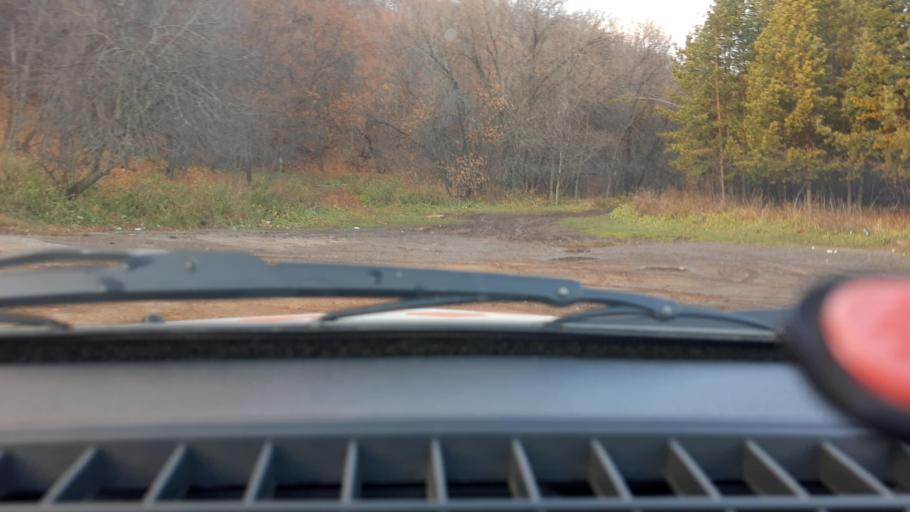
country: RU
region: Bashkortostan
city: Ufa
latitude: 54.7248
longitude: 56.0288
